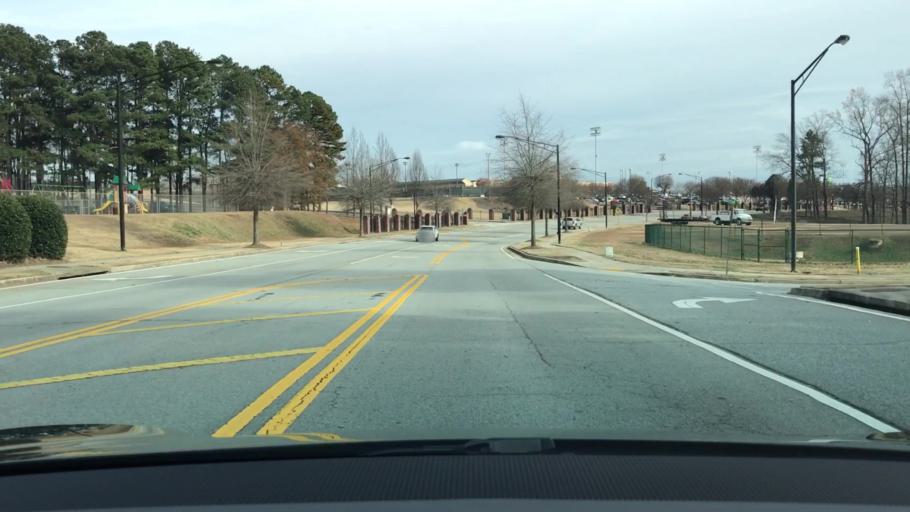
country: US
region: Georgia
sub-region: Gwinnett County
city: Buford
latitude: 34.1330
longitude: -83.9907
